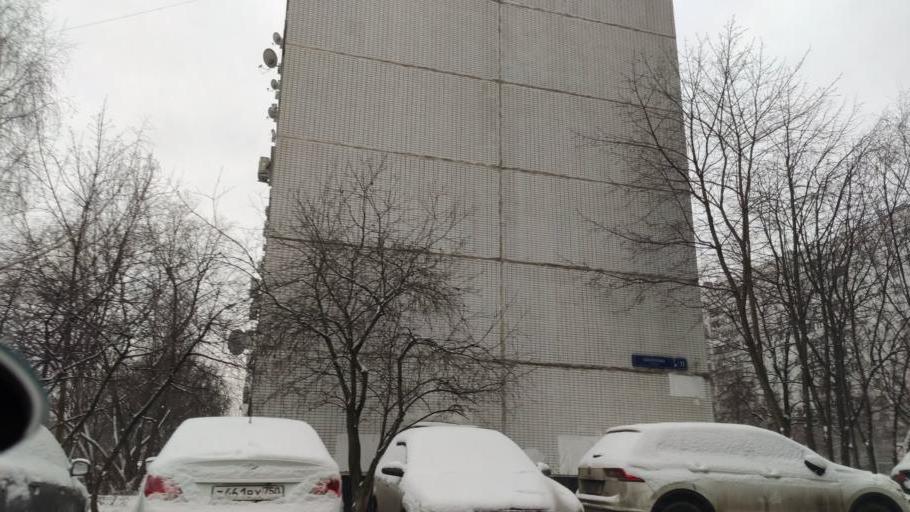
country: RU
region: Moscow
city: Novo-Peredelkino
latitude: 55.6407
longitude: 37.3474
